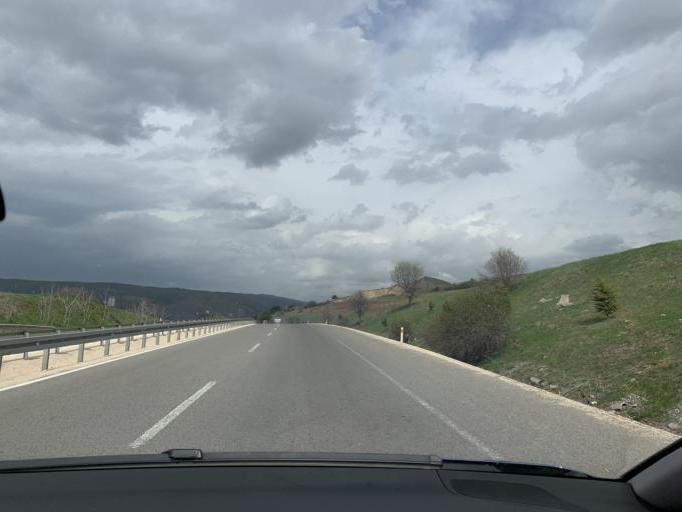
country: TR
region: Bolu
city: Yenicaga
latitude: 40.7824
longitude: 32.1015
